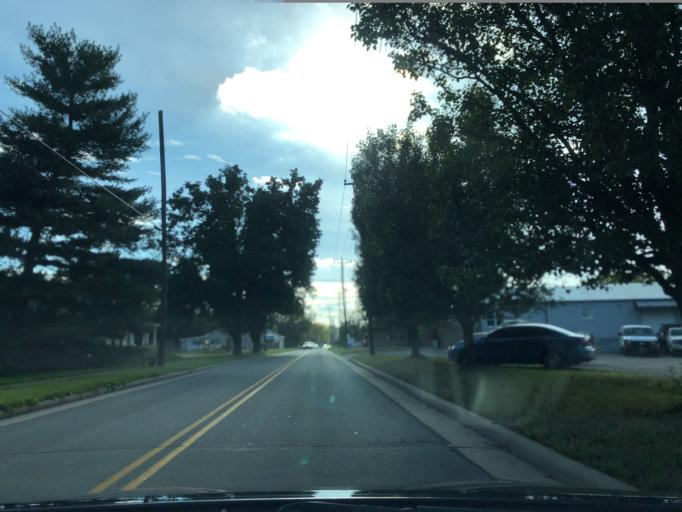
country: US
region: Ohio
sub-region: Hamilton County
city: Loveland
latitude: 39.2660
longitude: -84.2622
